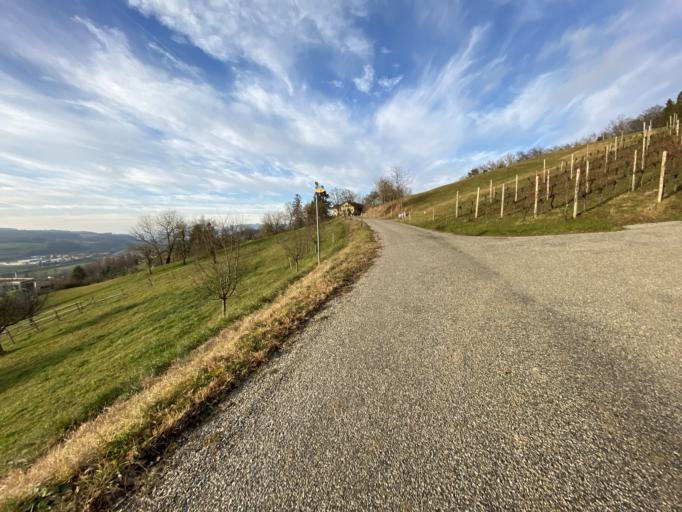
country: CH
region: Aargau
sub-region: Bezirk Laufenburg
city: Frick
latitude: 47.5119
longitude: 8.0320
